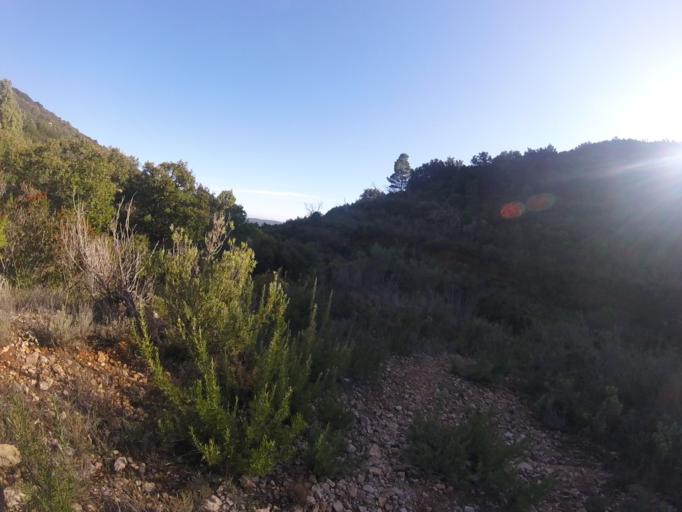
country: ES
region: Valencia
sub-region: Provincia de Castello
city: Sarratella
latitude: 40.2932
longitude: 0.0498
